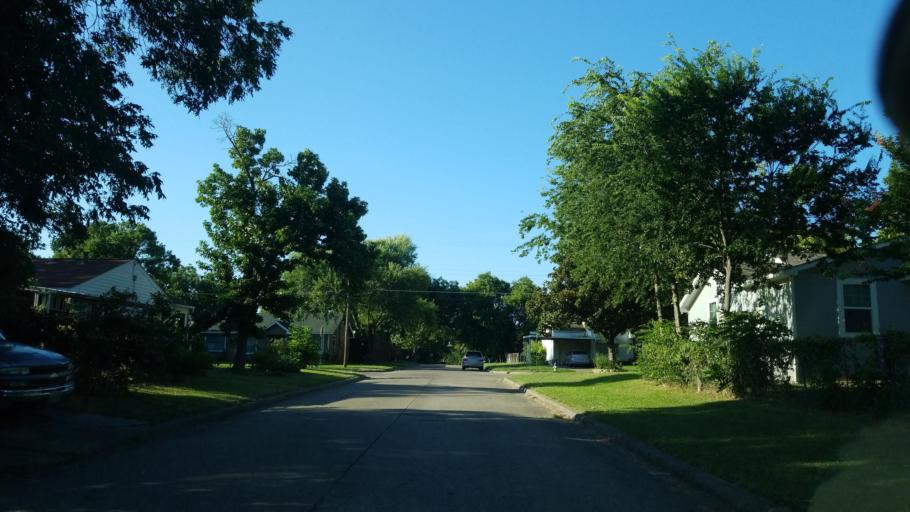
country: US
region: Texas
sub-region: Dallas County
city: Balch Springs
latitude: 32.7746
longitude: -96.7068
